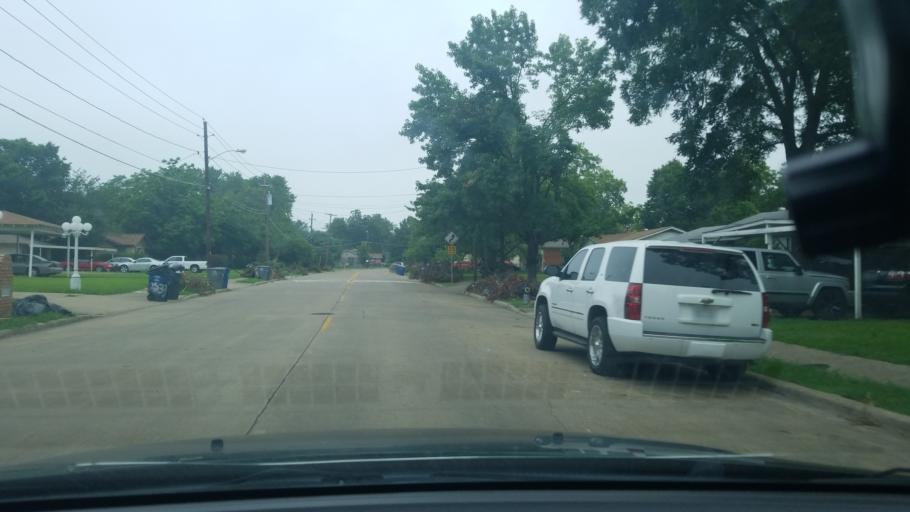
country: US
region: Texas
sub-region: Dallas County
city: Balch Springs
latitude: 32.7561
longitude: -96.6784
